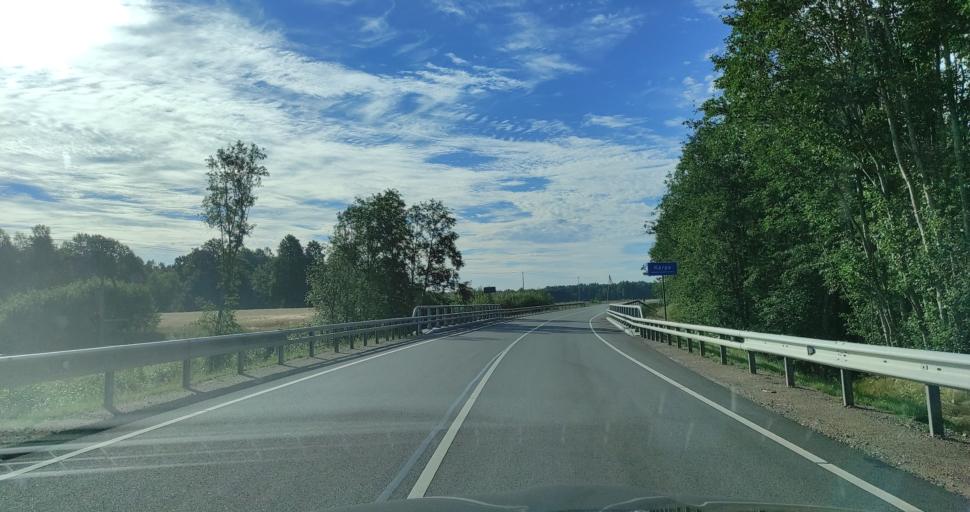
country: LV
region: Pavilostas
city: Pavilosta
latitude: 56.8324
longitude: 21.2200
